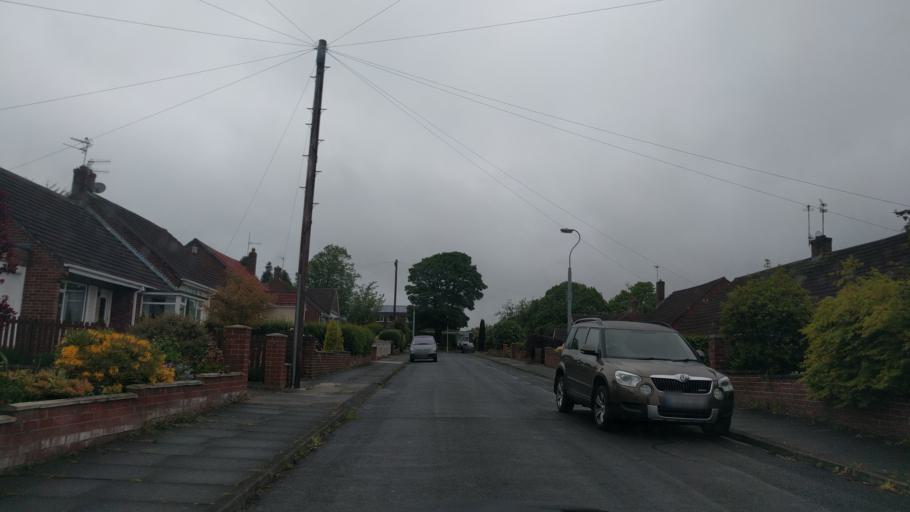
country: GB
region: England
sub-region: Northumberland
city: Morpeth
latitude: 55.1597
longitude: -1.6998
